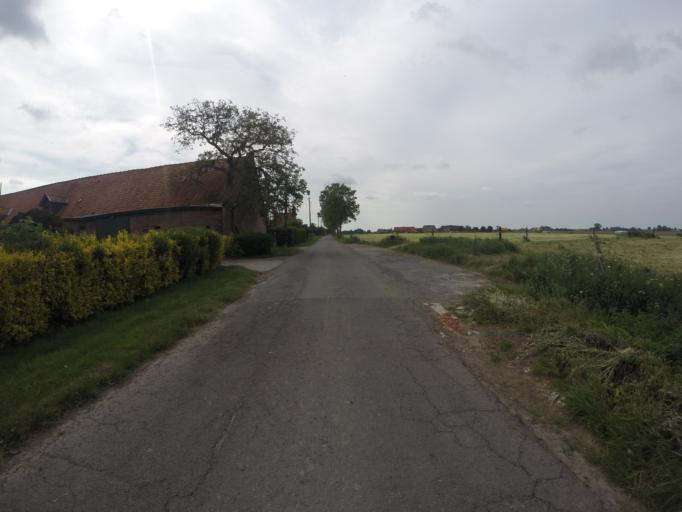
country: BE
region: Flanders
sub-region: Provincie West-Vlaanderen
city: Tielt
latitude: 51.0486
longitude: 3.3244
